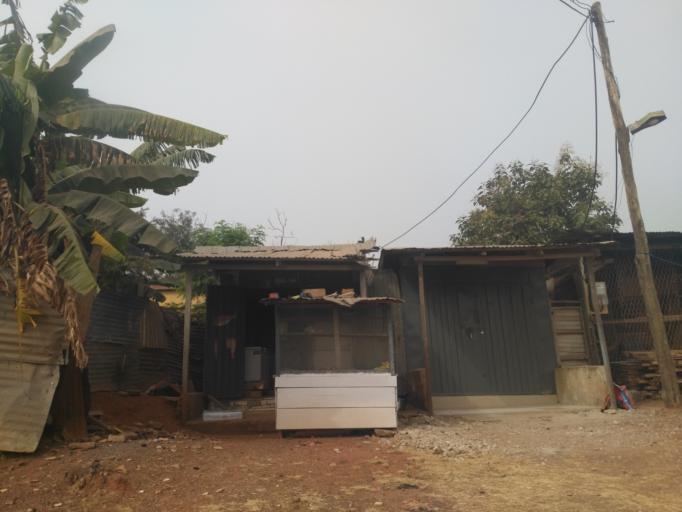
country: GH
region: Ashanti
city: Kumasi
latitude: 6.6652
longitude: -1.6147
